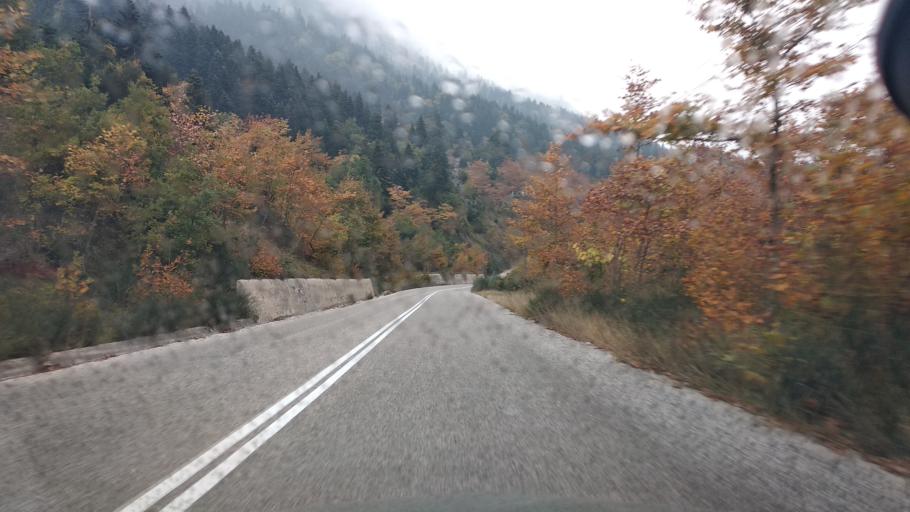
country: GR
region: Thessaly
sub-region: Trikala
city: Pyli
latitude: 39.4923
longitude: 21.5435
